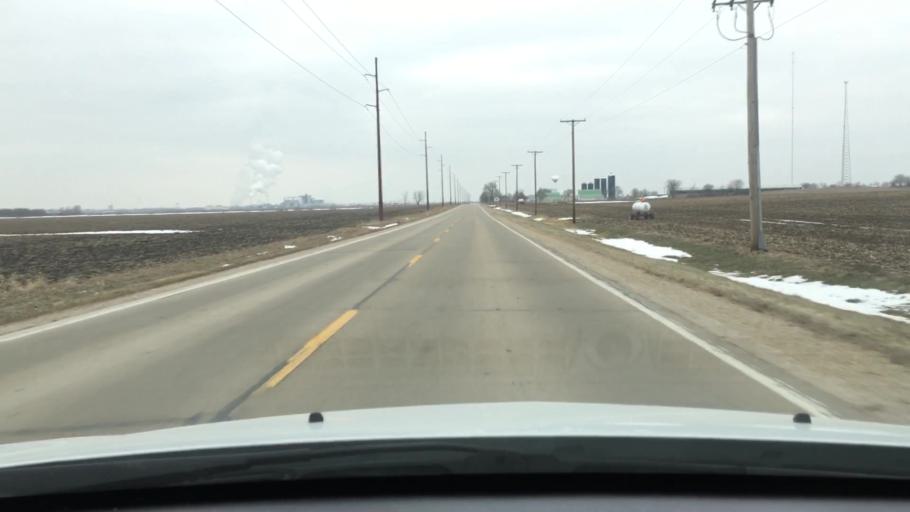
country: US
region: Illinois
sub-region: Ogle County
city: Rochelle
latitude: 41.8623
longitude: -89.0248
